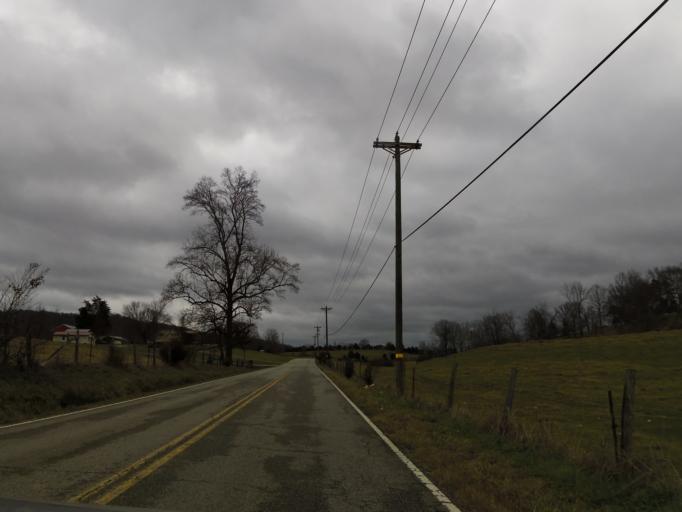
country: US
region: Tennessee
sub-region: Grainger County
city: Rutledge
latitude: 36.2019
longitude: -83.5469
